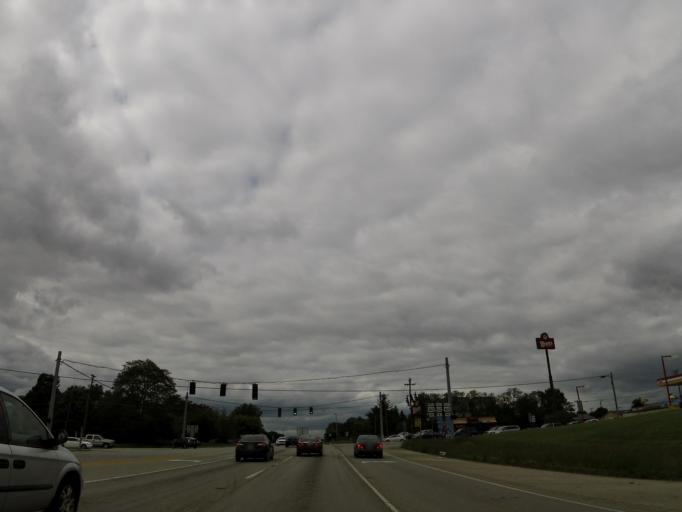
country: US
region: Kentucky
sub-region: Scott County
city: Georgetown
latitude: 38.2139
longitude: -84.5400
